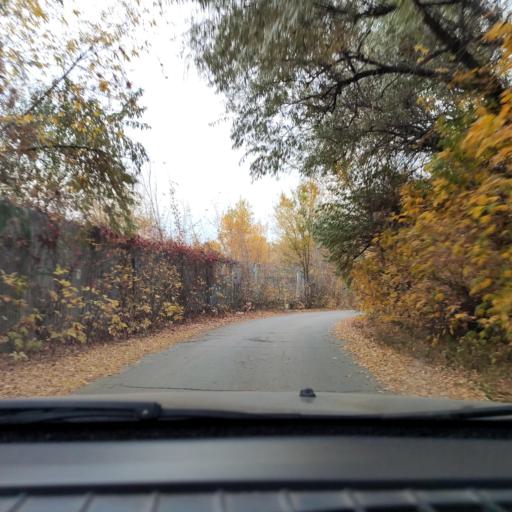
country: RU
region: Samara
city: Tol'yatti
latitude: 53.4976
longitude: 49.2628
